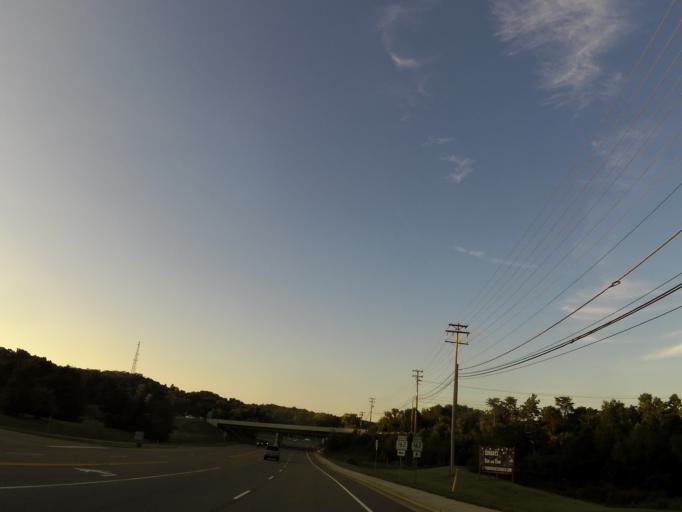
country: US
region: Tennessee
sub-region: Knox County
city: Farragut
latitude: 35.9332
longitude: -84.1454
